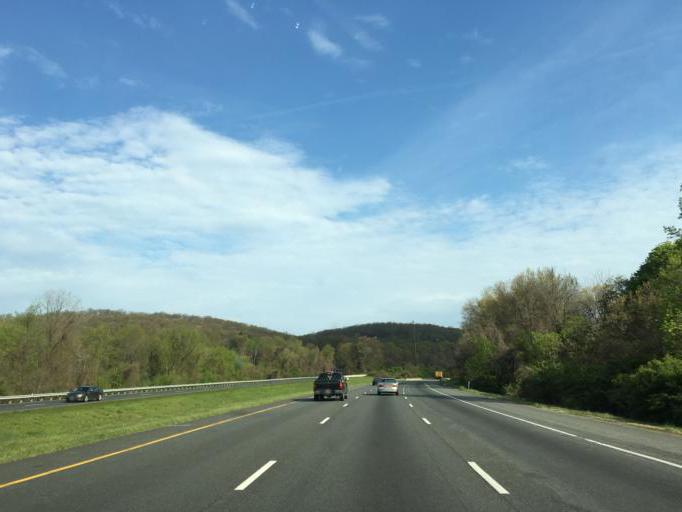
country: US
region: Maryland
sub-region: Frederick County
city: Braddock Heights
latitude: 39.4231
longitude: -77.4865
